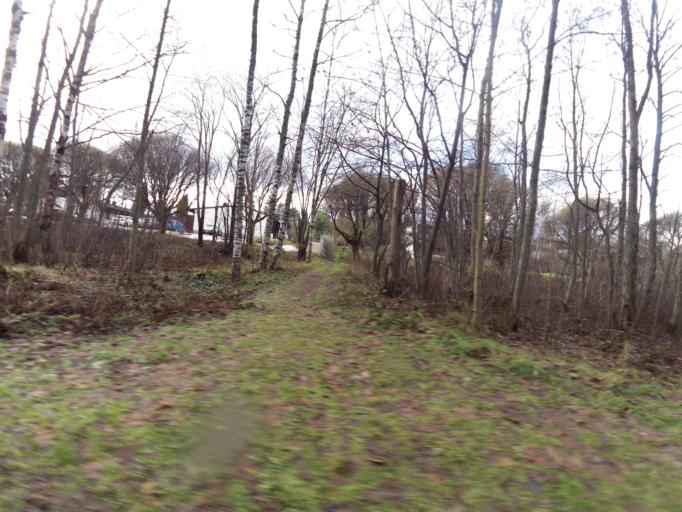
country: FI
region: Uusimaa
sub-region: Helsinki
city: Koukkuniemi
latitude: 60.1847
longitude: 24.7650
